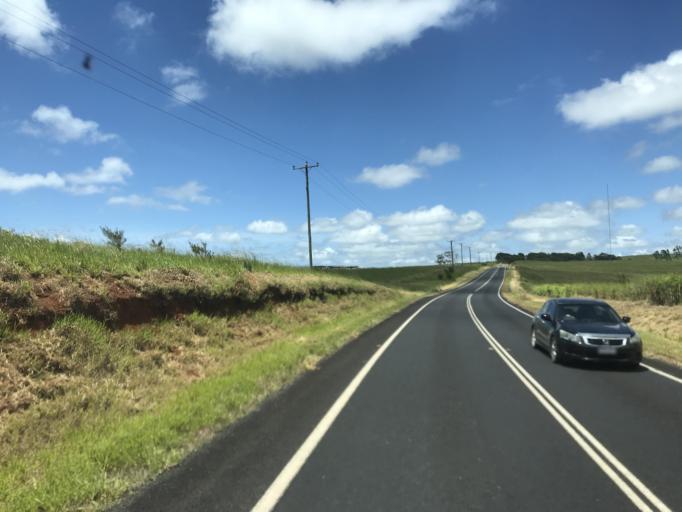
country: AU
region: Queensland
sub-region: Tablelands
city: Ravenshoe
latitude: -17.4905
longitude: 145.4737
